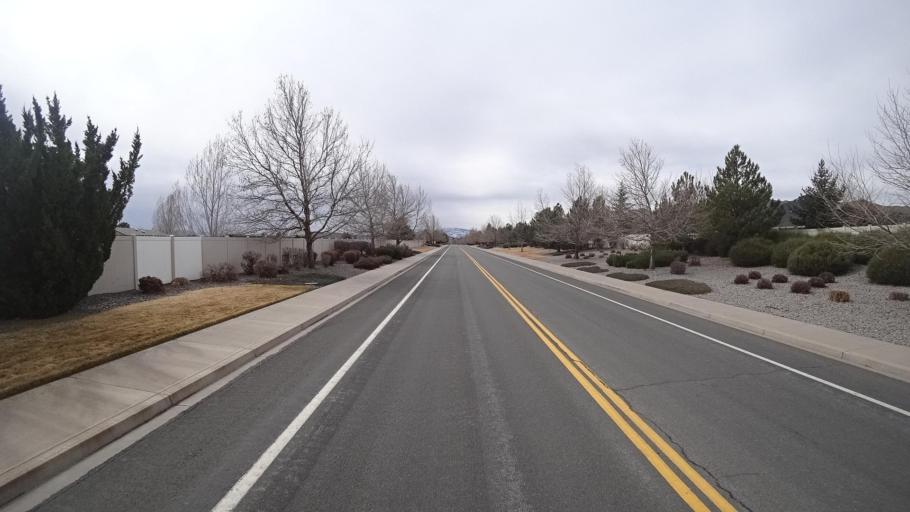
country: US
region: Nevada
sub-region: Washoe County
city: Spanish Springs
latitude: 39.6624
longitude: -119.7251
